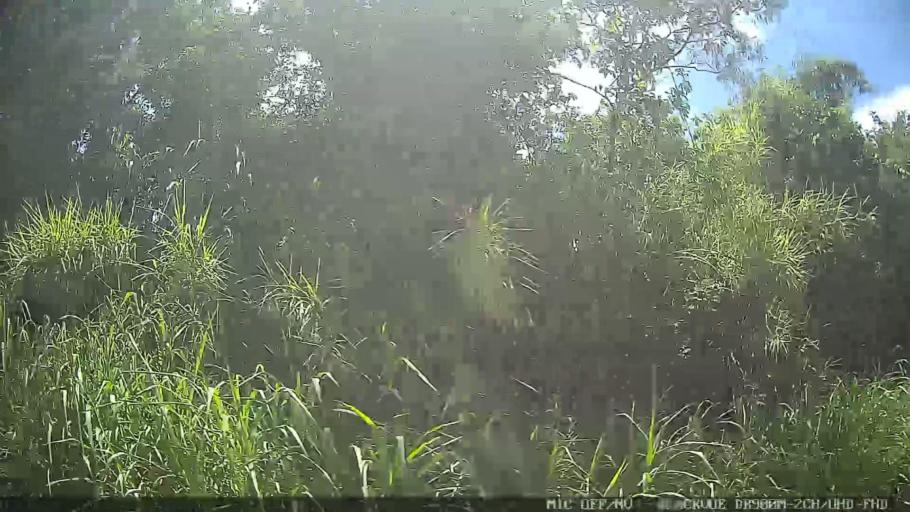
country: BR
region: Sao Paulo
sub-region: Laranjal Paulista
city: Laranjal Paulista
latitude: -23.0267
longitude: -47.8441
